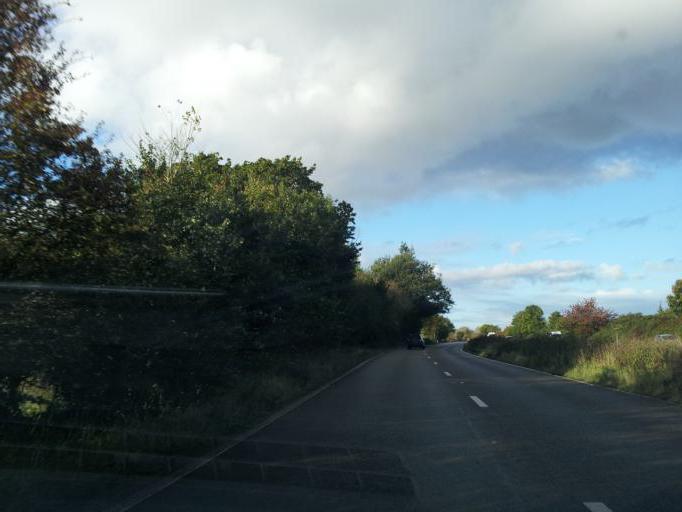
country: GB
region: England
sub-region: Norfolk
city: Brundall
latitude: 52.6307
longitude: 1.4141
